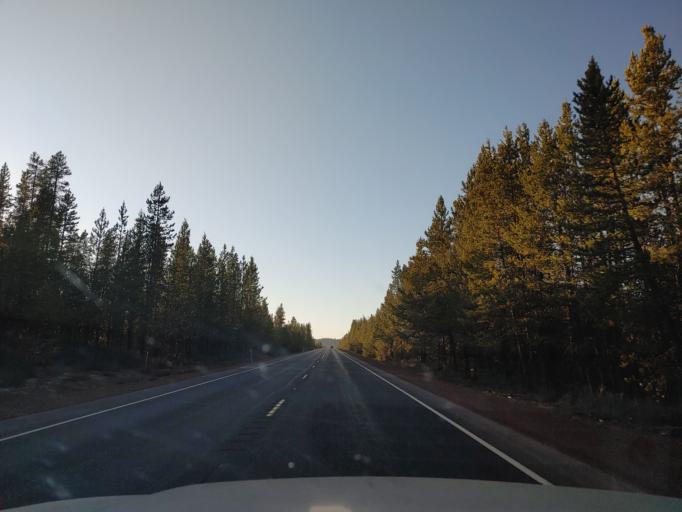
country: US
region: Oregon
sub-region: Deschutes County
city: La Pine
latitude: 43.4220
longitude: -121.8427
